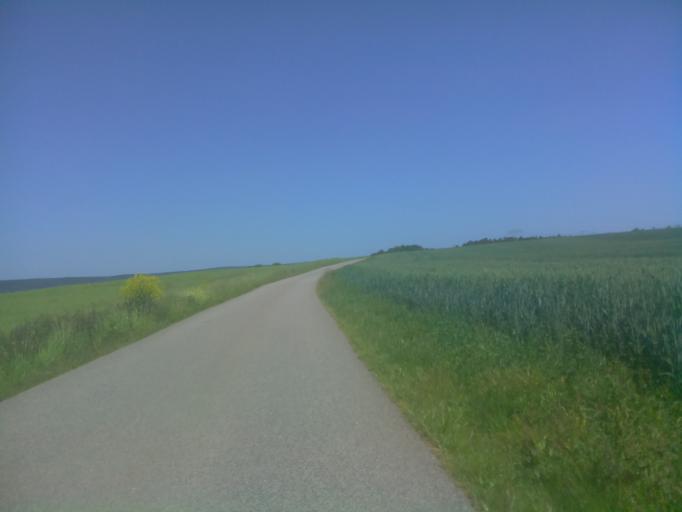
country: DE
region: Thuringia
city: Saalfeld
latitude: 50.6350
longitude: 11.3957
